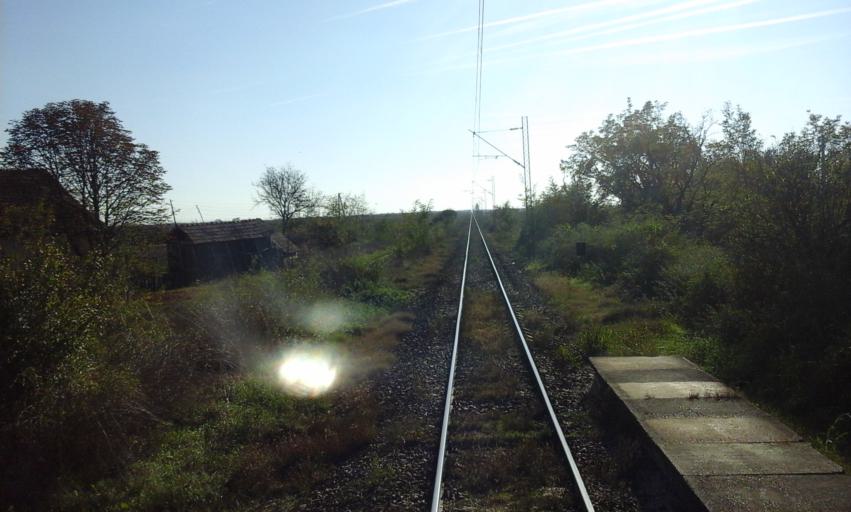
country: RS
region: Autonomna Pokrajina Vojvodina
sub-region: Severnobacki Okrug
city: Subotica
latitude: 45.9860
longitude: 19.6754
